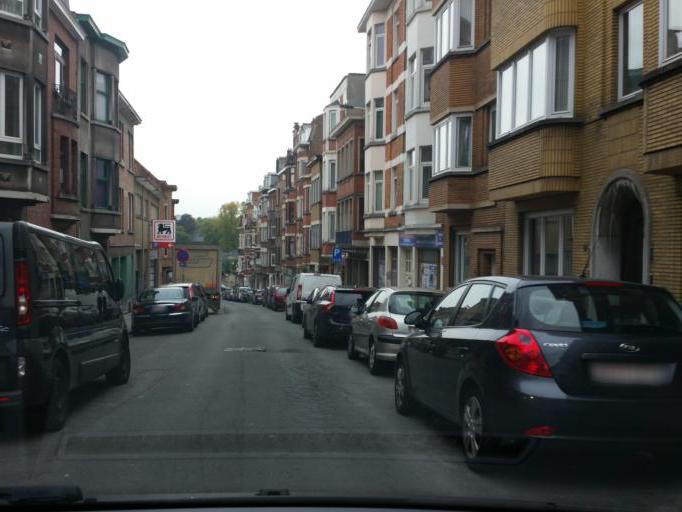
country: BE
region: Flanders
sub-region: Provincie Vlaams-Brabant
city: Drogenbos
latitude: 50.8086
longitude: 4.3186
